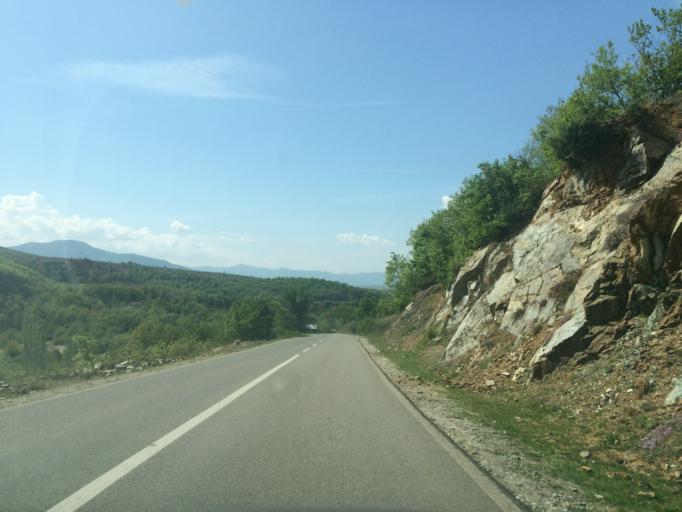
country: AL
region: Kukes
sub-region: Rrethi i Tropojes
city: Llugaj
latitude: 42.3785
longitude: 20.1303
